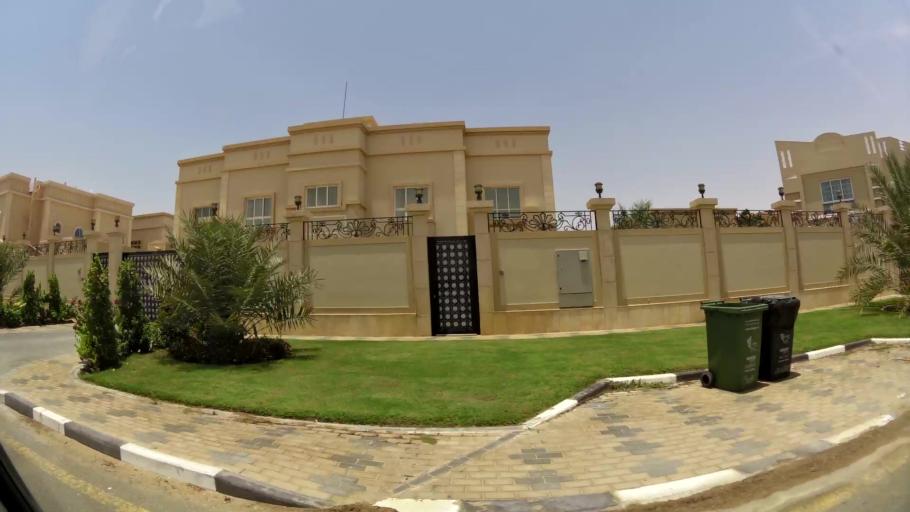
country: AE
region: Ash Shariqah
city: Sharjah
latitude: 25.2343
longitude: 55.4629
